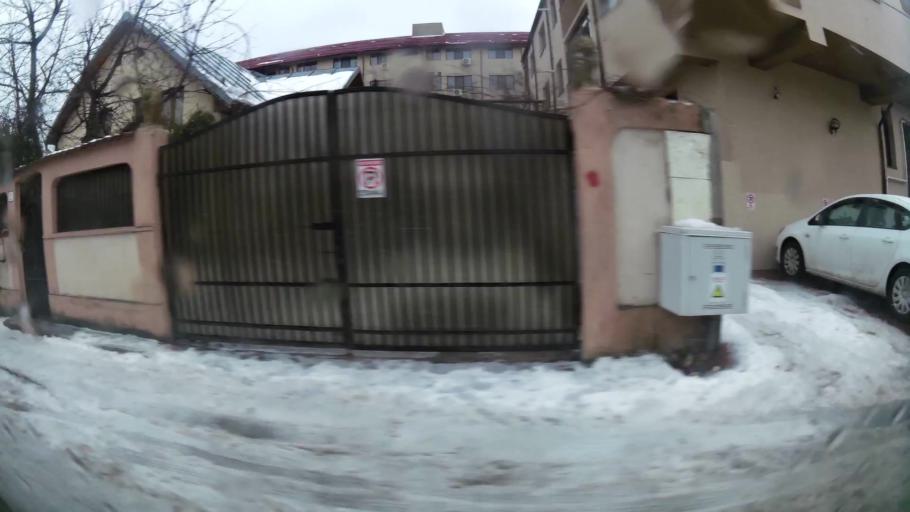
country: RO
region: Ilfov
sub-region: Comuna Chiajna
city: Rosu
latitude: 44.4285
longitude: 26.0121
